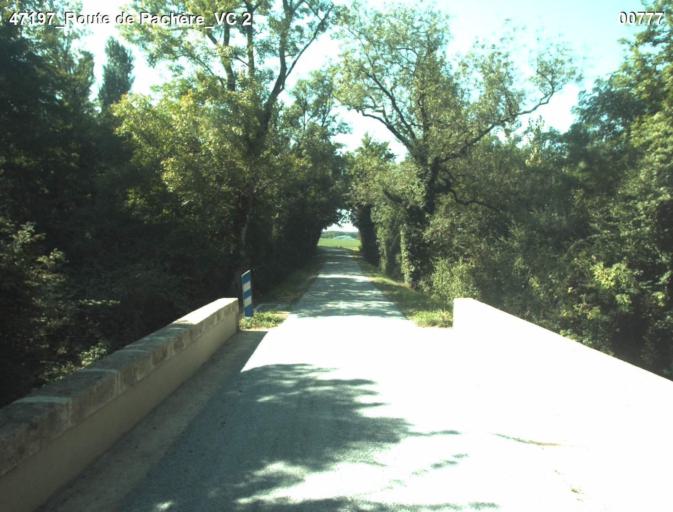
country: FR
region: Aquitaine
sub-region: Departement du Lot-et-Garonne
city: Laplume
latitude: 44.0910
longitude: 0.4632
